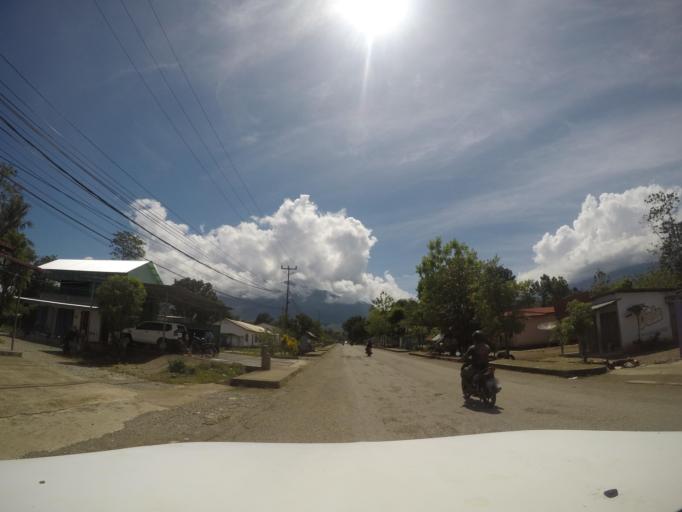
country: TL
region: Bobonaro
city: Maliana
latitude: -8.9891
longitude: 125.2116
